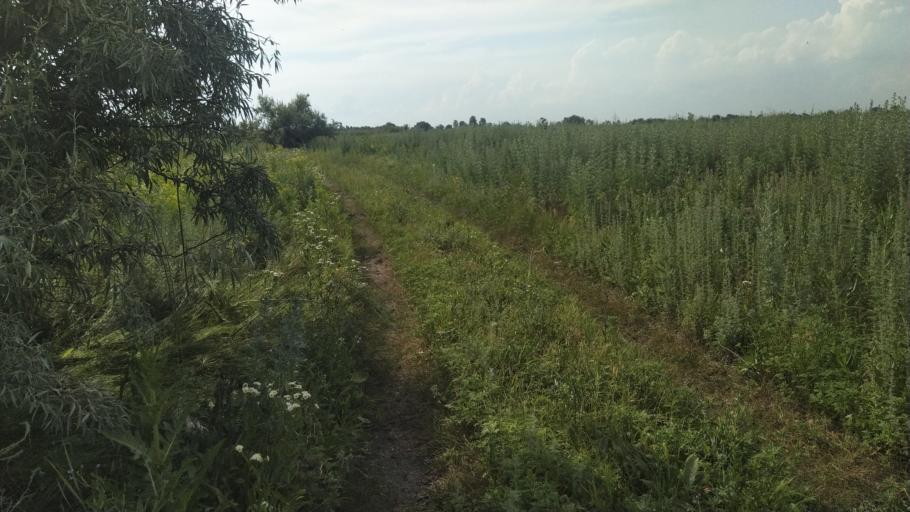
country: RU
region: Rostov
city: Kuleshovka
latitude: 47.1261
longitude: 39.6191
